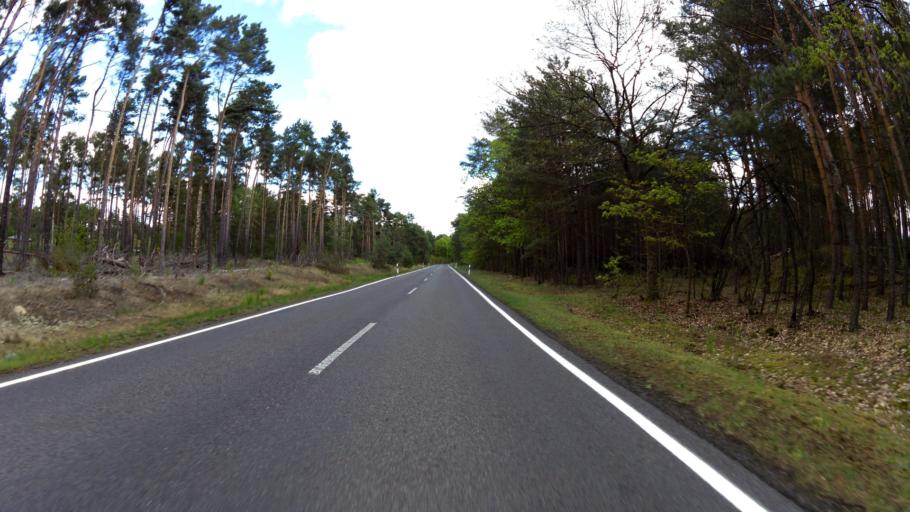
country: DE
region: Brandenburg
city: Schlepzig
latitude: 52.1011
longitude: 13.9129
